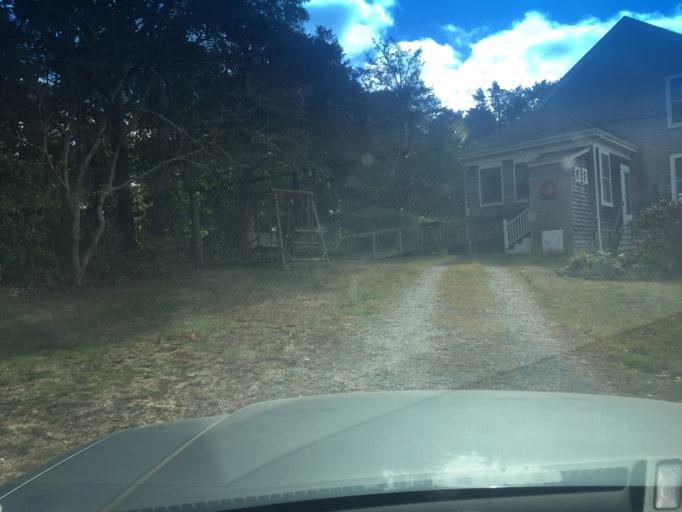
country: US
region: Massachusetts
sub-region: Barnstable County
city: Pocasset
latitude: 41.6945
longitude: -70.6170
